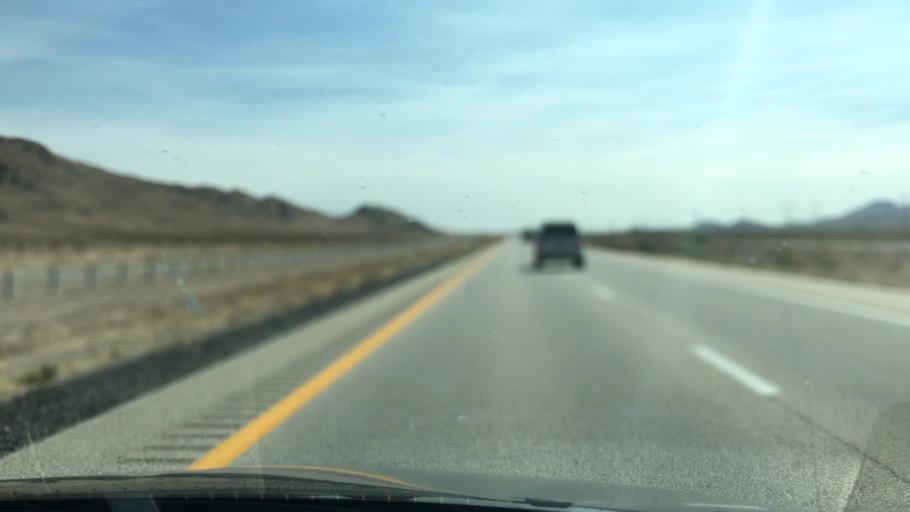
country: US
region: Nevada
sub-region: Clark County
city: Nellis Air Force Base
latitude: 36.4021
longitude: -114.8788
